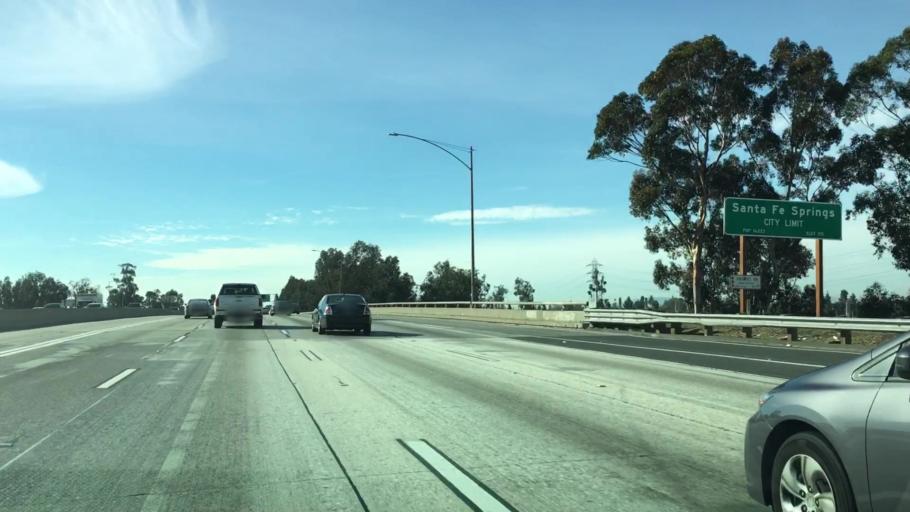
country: US
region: California
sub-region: Los Angeles County
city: West Whittier-Los Nietos
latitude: 33.9660
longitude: -118.0840
